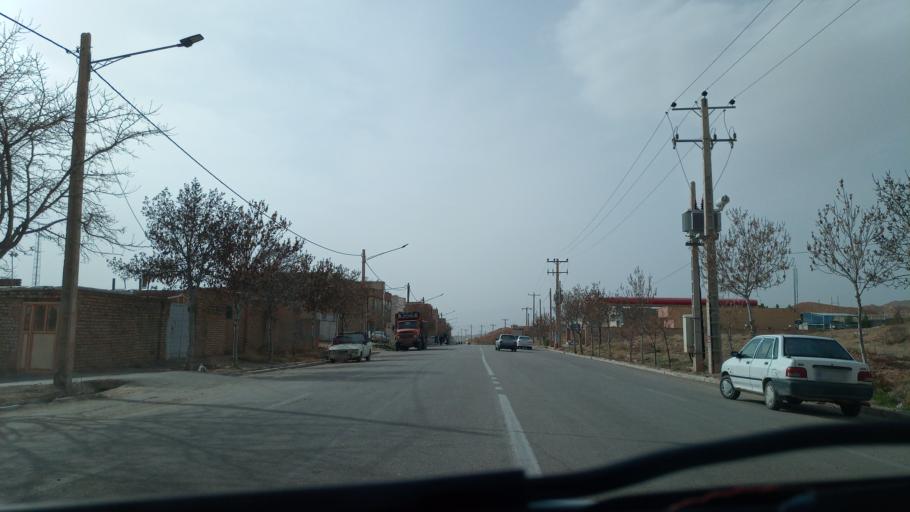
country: IR
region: Khorasan-e Shomali
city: Esfarayen
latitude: 37.0865
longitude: 57.4982
